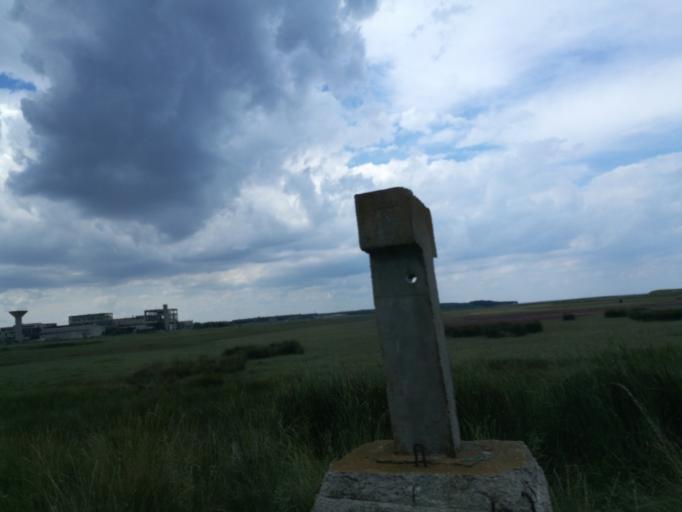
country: RO
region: Constanta
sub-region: Comuna Sacele
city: Sacele
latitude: 44.4439
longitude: 28.7491
